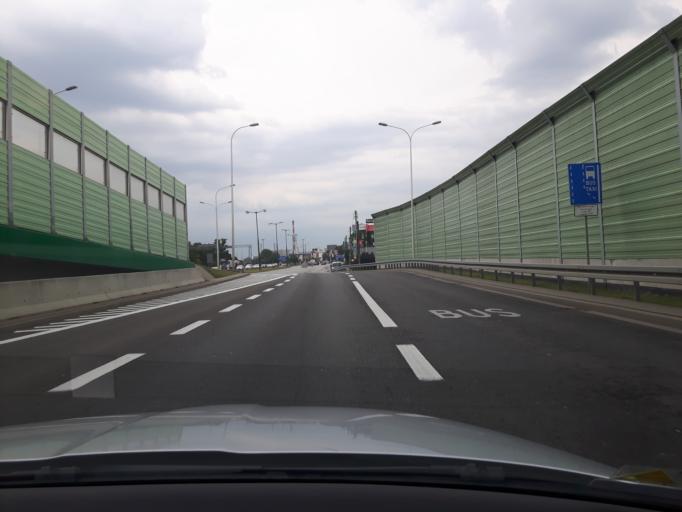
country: PL
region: Masovian Voivodeship
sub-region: Warszawa
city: Bialoleka
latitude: 52.3150
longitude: 20.9761
